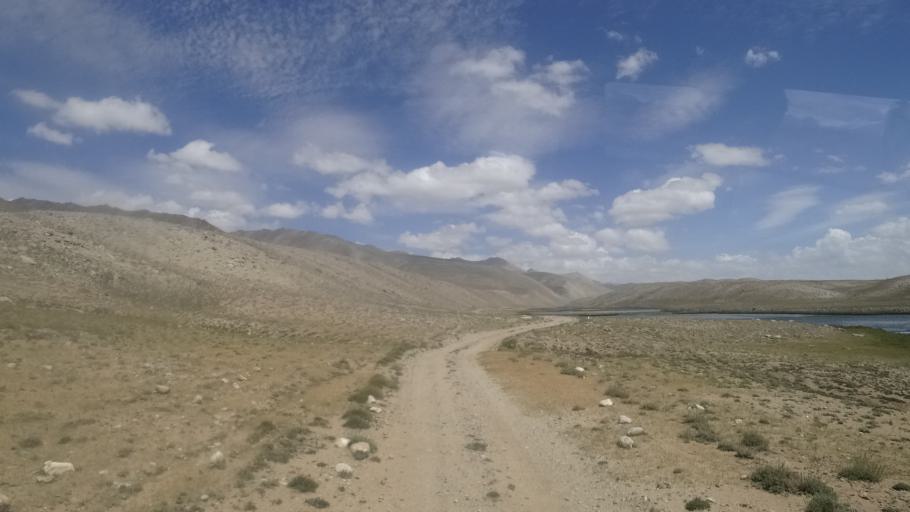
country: TJ
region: Gorno-Badakhshan
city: Murghob
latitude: 37.4688
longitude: 73.4256
